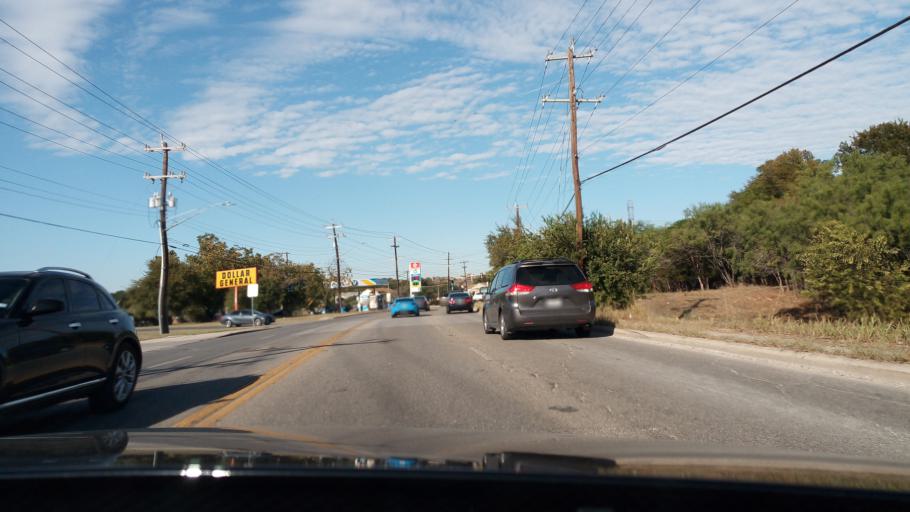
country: US
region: Texas
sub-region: Bexar County
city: Windcrest
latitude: 29.5330
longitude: -98.4295
